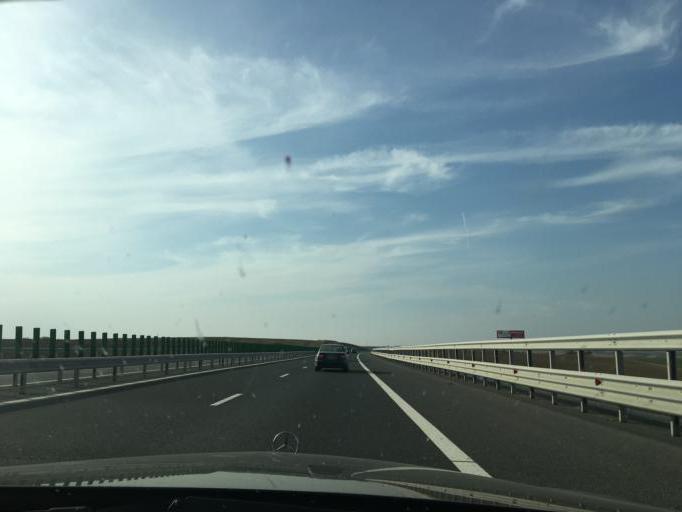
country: RO
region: Constanta
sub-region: Comuna Saligny
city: Saligny
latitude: 44.2440
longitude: 28.0916
